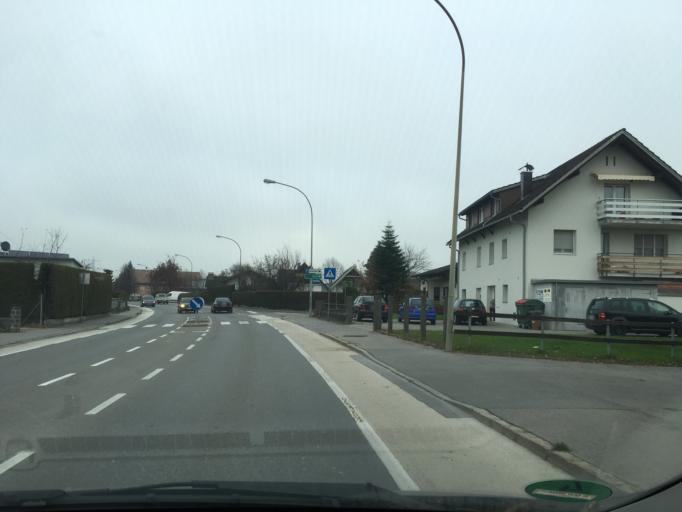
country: AT
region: Vorarlberg
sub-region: Politischer Bezirk Dornbirn
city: Hohenems
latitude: 47.3650
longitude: 9.6708
